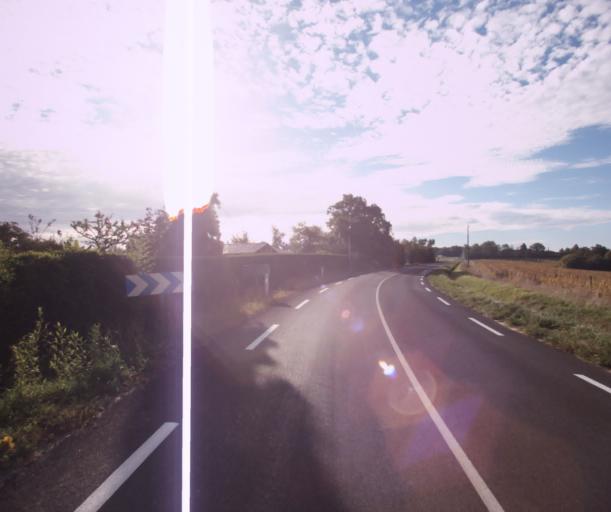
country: FR
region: Midi-Pyrenees
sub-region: Departement du Gers
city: Eauze
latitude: 43.8804
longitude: 0.0302
